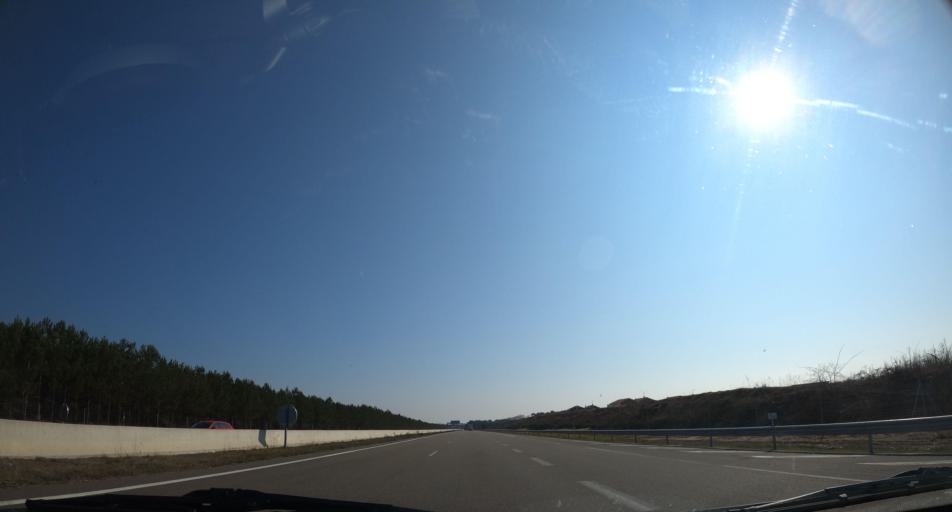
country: FR
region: Aquitaine
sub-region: Departement des Landes
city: Saint-Geours-de-Maremne
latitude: 43.6962
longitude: -1.2228
